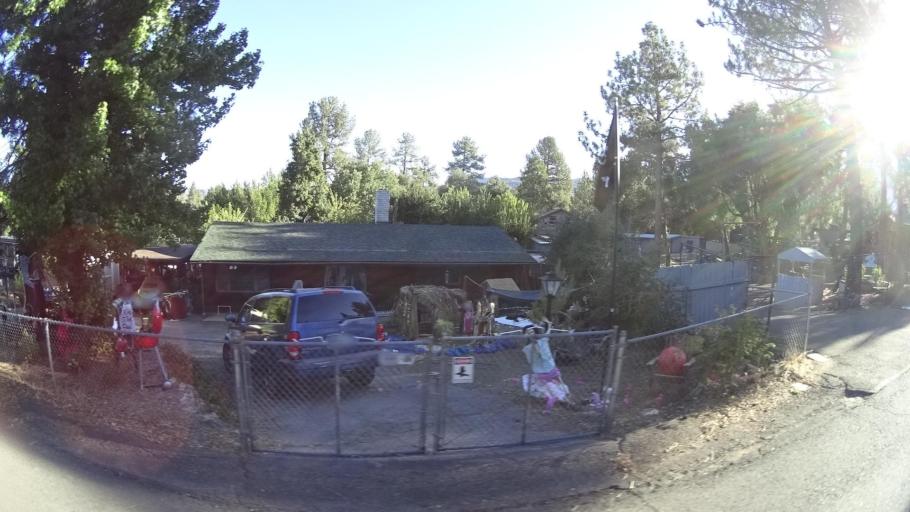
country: US
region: California
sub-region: San Diego County
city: Pine Valley
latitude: 32.8191
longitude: -116.5300
